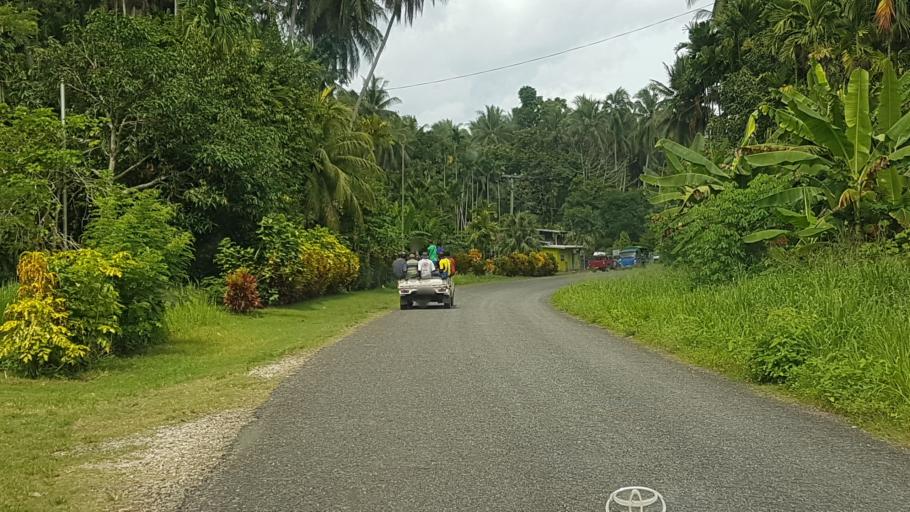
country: PG
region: Madang
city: Madang
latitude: -4.8094
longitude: 145.7522
